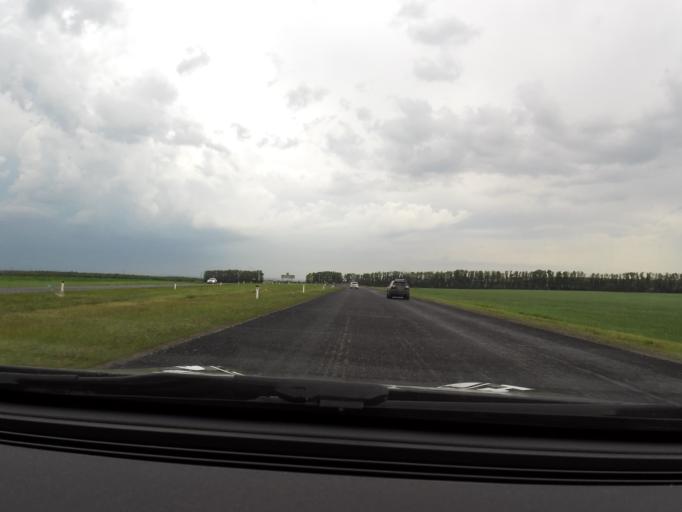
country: RU
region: Bashkortostan
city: Asanovo
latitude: 54.9519
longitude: 55.5842
